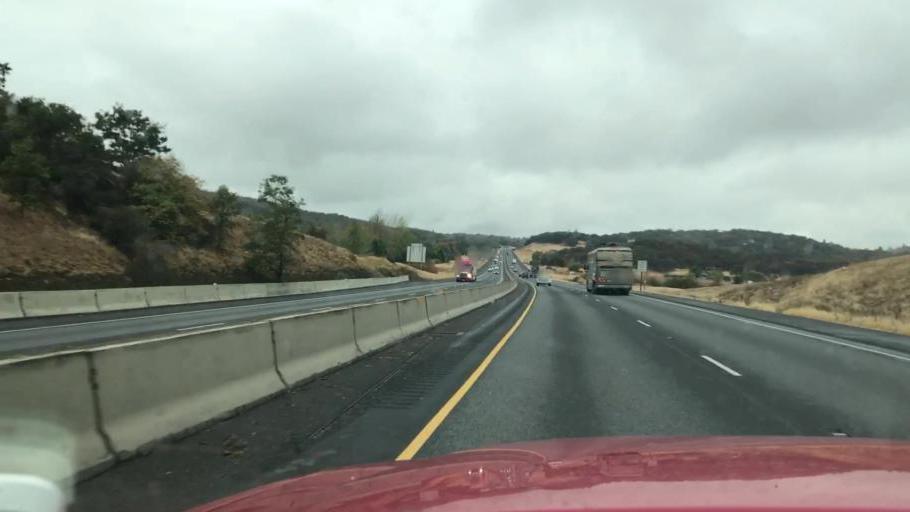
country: US
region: Oregon
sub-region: Jackson County
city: Central Point
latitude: 42.4127
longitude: -122.9646
